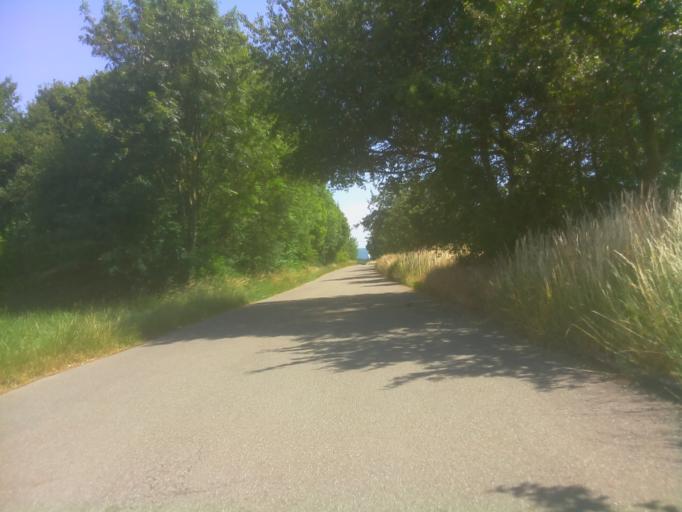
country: DE
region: Baden-Wuerttemberg
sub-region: Karlsruhe Region
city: Hemsbach
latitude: 49.5616
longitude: 8.6162
